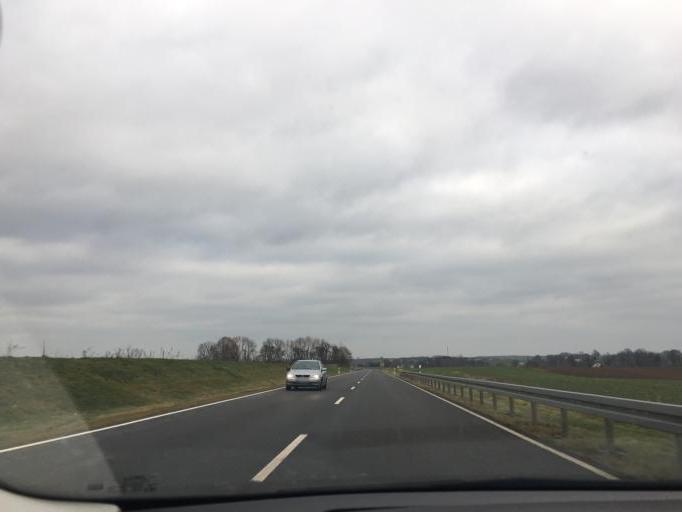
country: DE
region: Saxony
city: Niederfrohna
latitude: 50.8873
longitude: 12.7130
